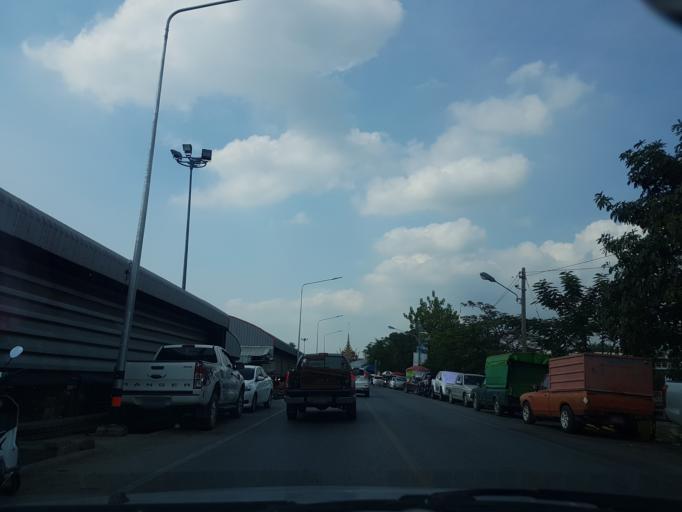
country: TH
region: Phra Nakhon Si Ayutthaya
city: Phachi
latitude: 14.3955
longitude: 100.7942
